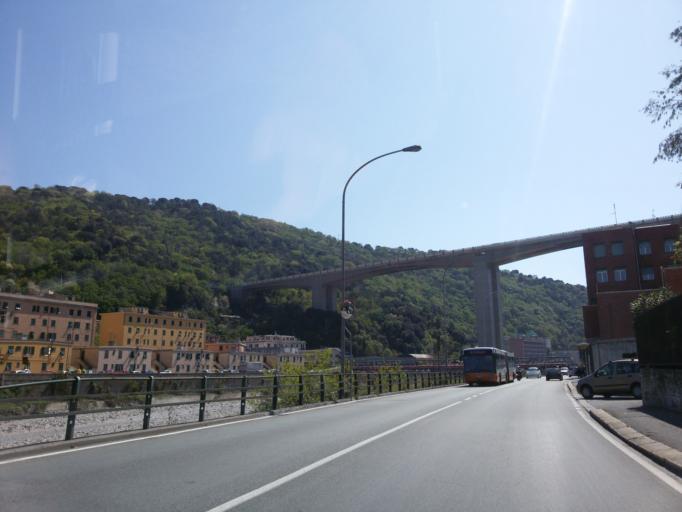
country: IT
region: Liguria
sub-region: Provincia di Genova
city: Genoa
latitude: 44.4356
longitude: 8.9618
